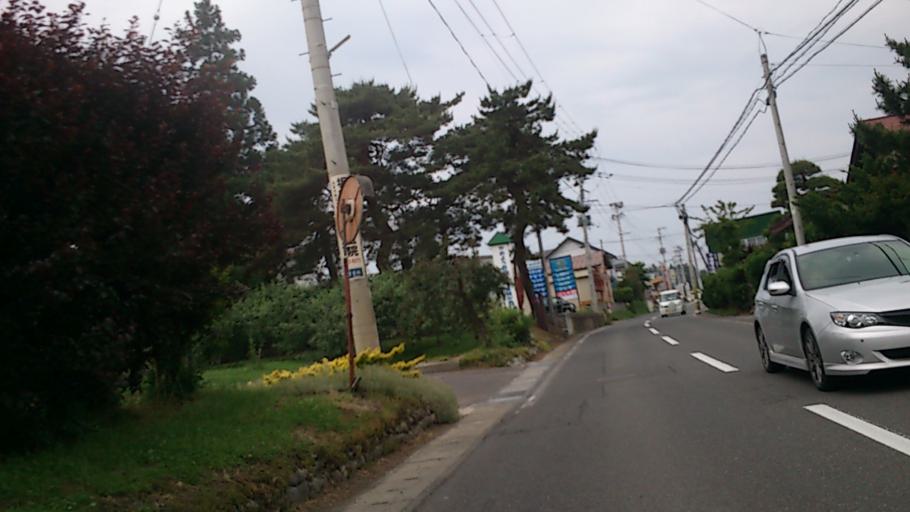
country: JP
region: Aomori
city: Hirosaki
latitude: 40.5937
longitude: 140.4464
